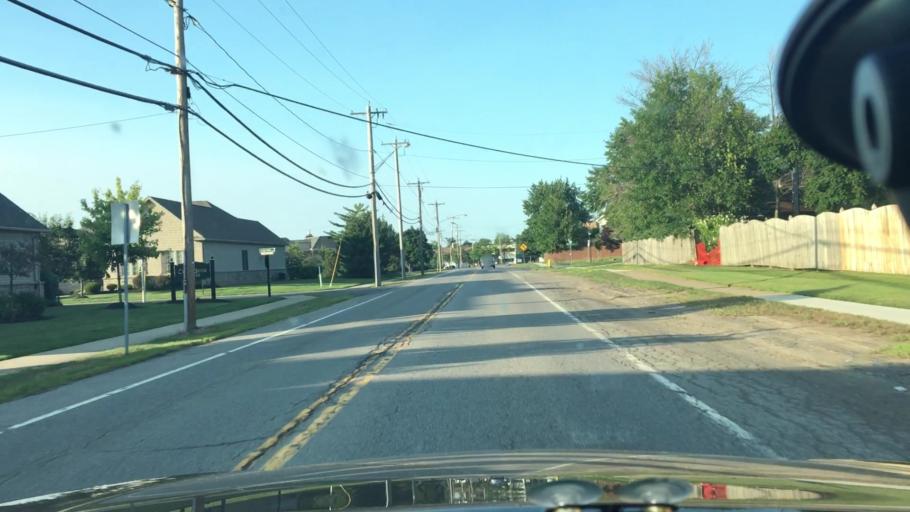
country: US
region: New York
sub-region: Erie County
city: Williamsville
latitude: 42.9878
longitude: -78.7618
